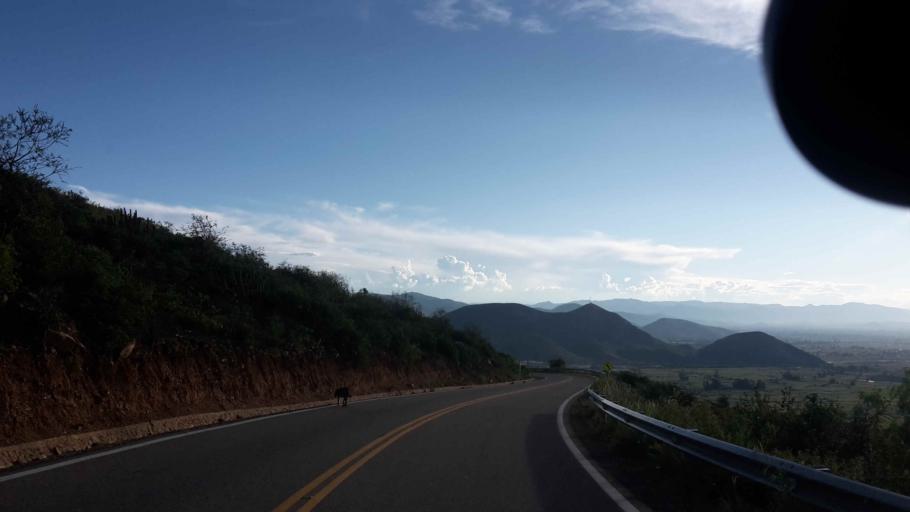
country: BO
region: Cochabamba
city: Arani
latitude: -17.5877
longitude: -65.7523
